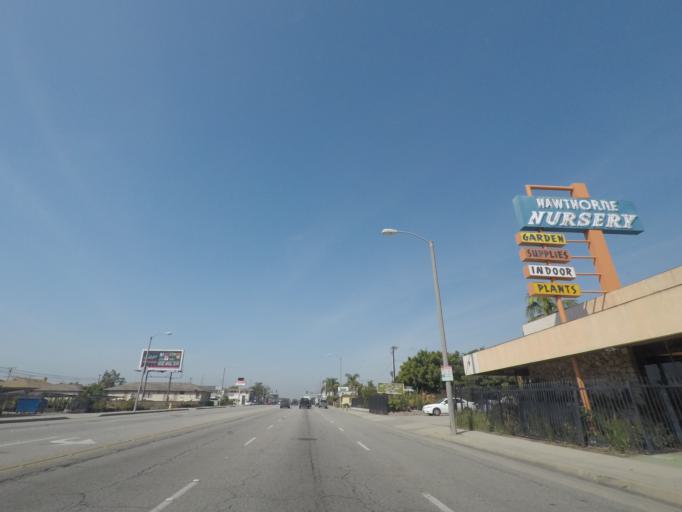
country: US
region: California
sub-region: Los Angeles County
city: Hawthorne
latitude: 33.9165
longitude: -118.3550
